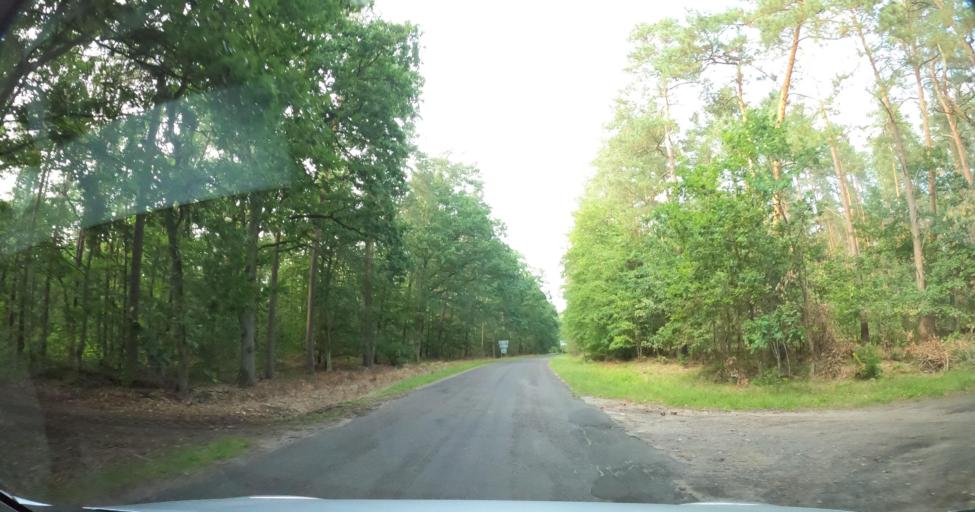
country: PL
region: West Pomeranian Voivodeship
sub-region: Powiat goleniowski
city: Goleniow
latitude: 53.5092
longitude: 14.8656
